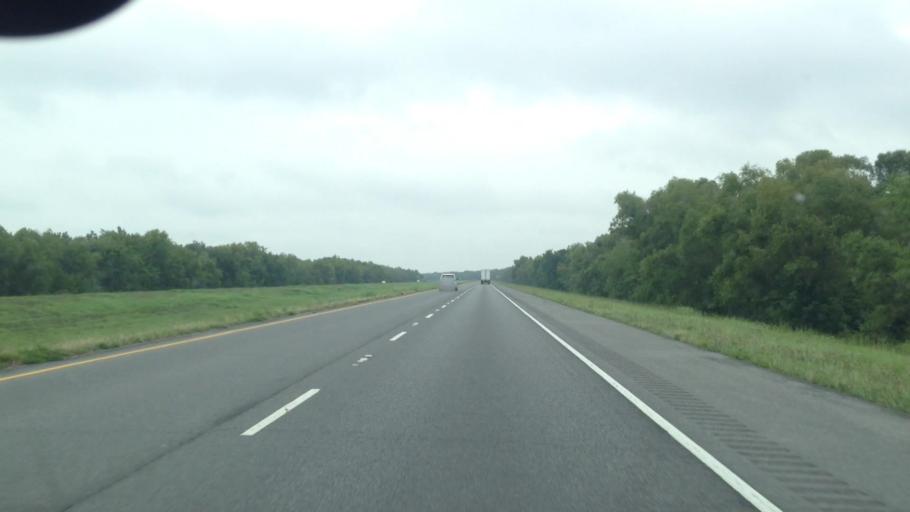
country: US
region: Louisiana
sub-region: Saint Landry Parish
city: Opelousas
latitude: 30.6785
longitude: -92.0750
